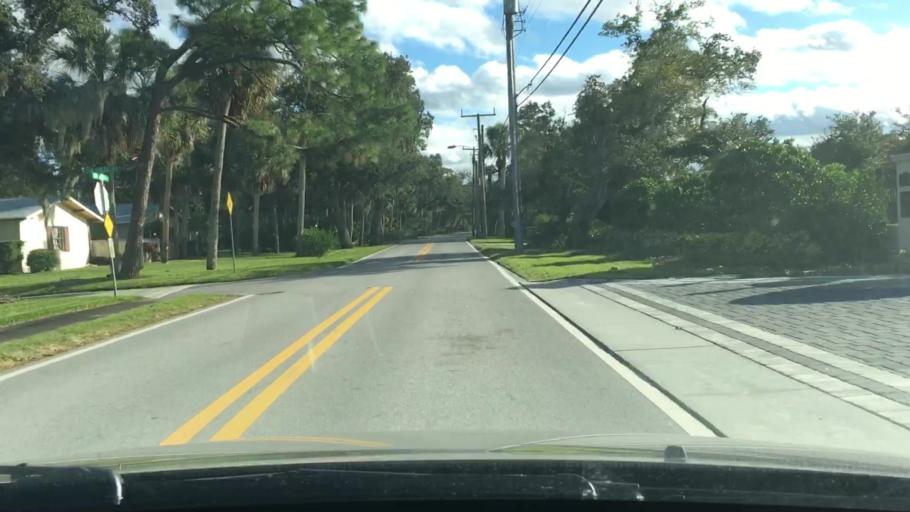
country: US
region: Florida
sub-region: Volusia County
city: Ormond Beach
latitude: 29.3027
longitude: -81.0540
